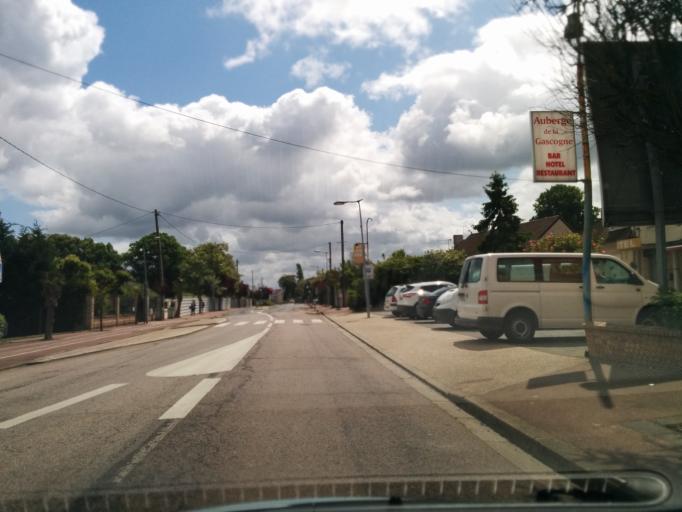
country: FR
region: Ile-de-France
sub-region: Departement des Yvelines
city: Porcheville
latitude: 48.9731
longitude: 1.7741
